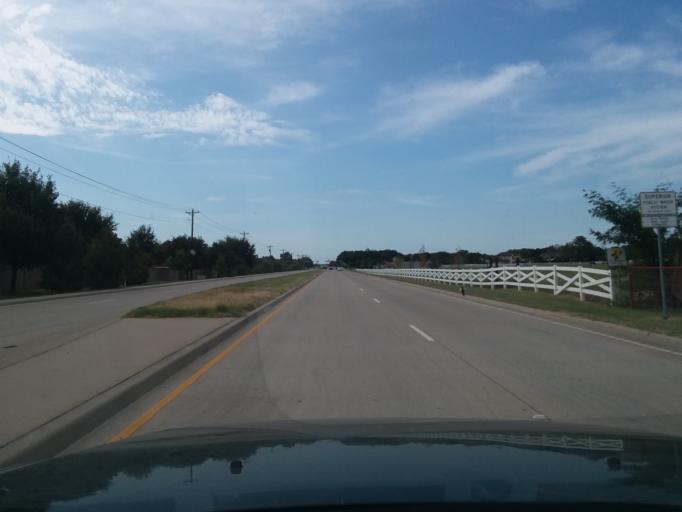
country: US
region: Texas
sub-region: Denton County
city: Bartonville
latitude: 33.0986
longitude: -97.1313
